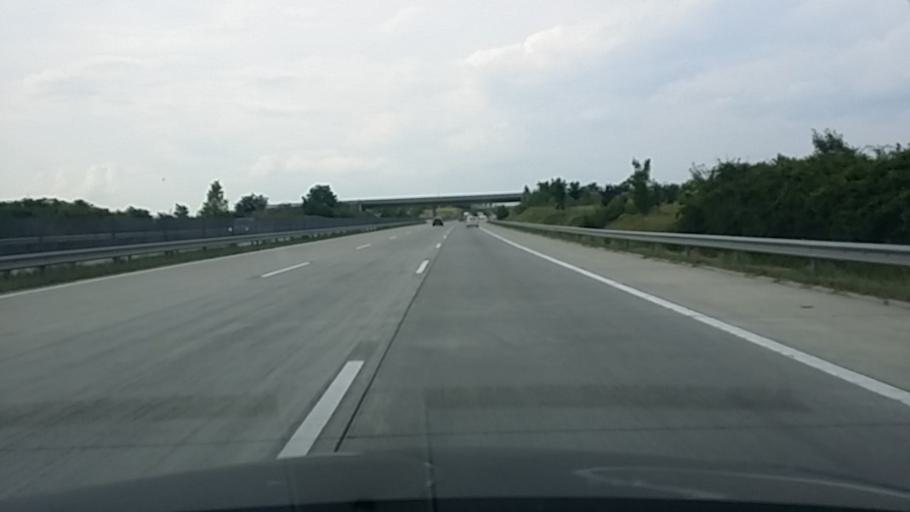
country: HU
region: Pest
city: Nagytarcsa
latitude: 47.5290
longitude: 19.3044
